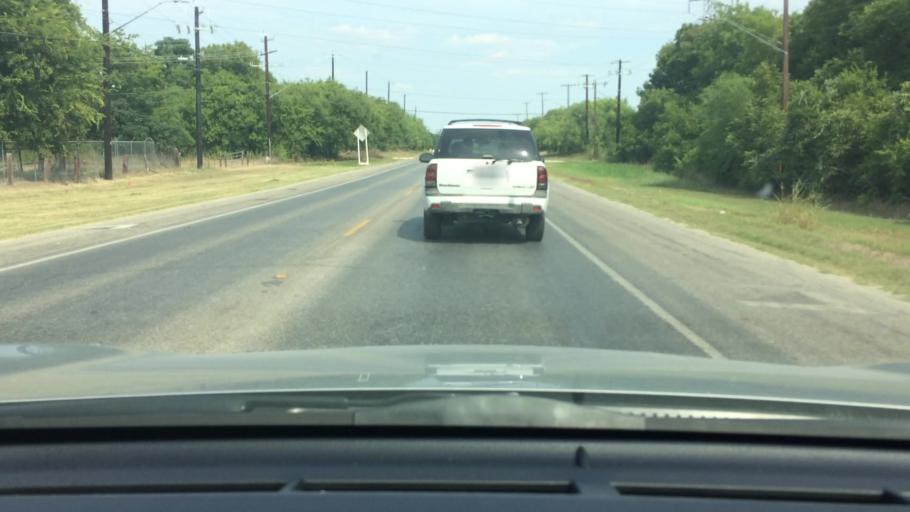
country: US
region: Texas
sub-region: Bexar County
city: San Antonio
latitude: 29.3337
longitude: -98.4502
